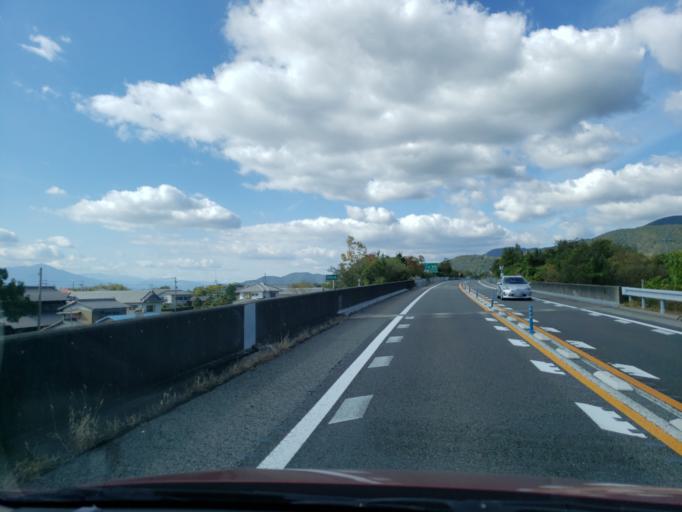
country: JP
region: Tokushima
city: Kamojimacho-jogejima
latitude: 34.1214
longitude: 134.3704
